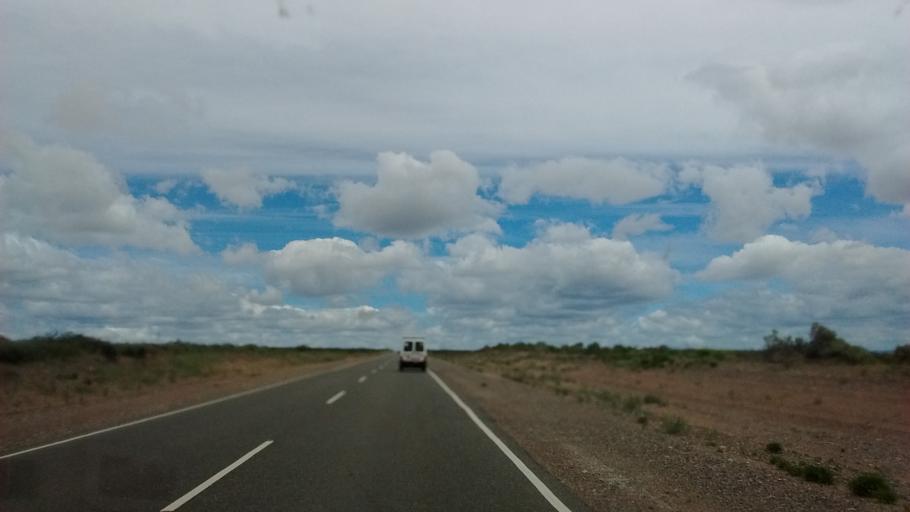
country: AR
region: Neuquen
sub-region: Departamento de Picun Leufu
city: Picun Leufu
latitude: -39.7523
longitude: -69.6306
